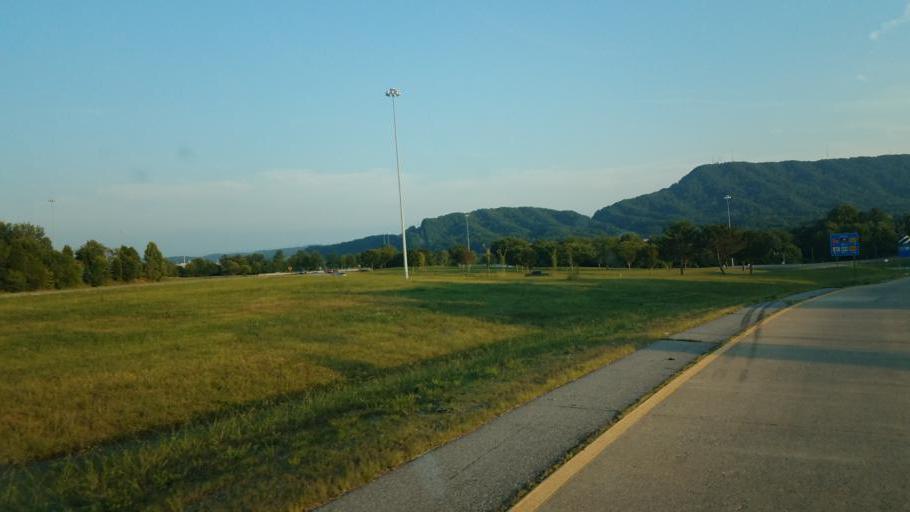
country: US
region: Tennessee
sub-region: Sullivan County
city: Kingsport
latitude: 36.5594
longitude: -82.5838
